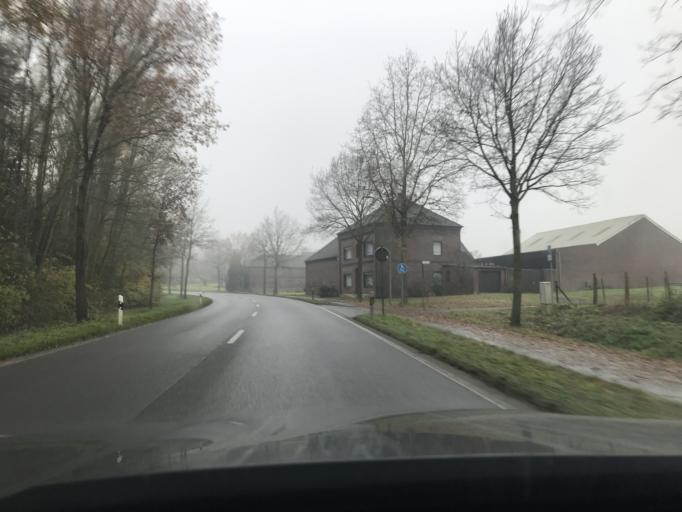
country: DE
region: North Rhine-Westphalia
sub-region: Regierungsbezirk Dusseldorf
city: Grefrath
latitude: 51.3221
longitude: 6.3226
